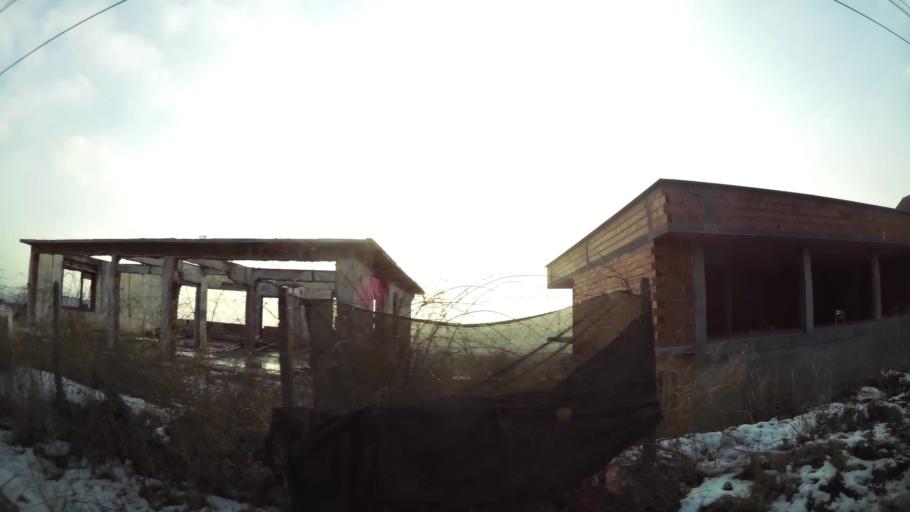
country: MK
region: Aracinovo
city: Arachinovo
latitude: 42.0257
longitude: 21.5640
